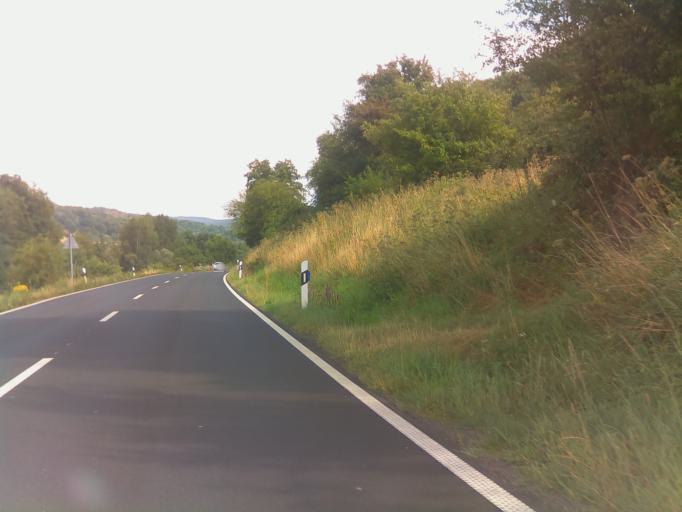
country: DE
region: Hesse
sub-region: Regierungsbezirk Darmstadt
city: Wachtersbach
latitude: 50.2379
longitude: 9.3150
